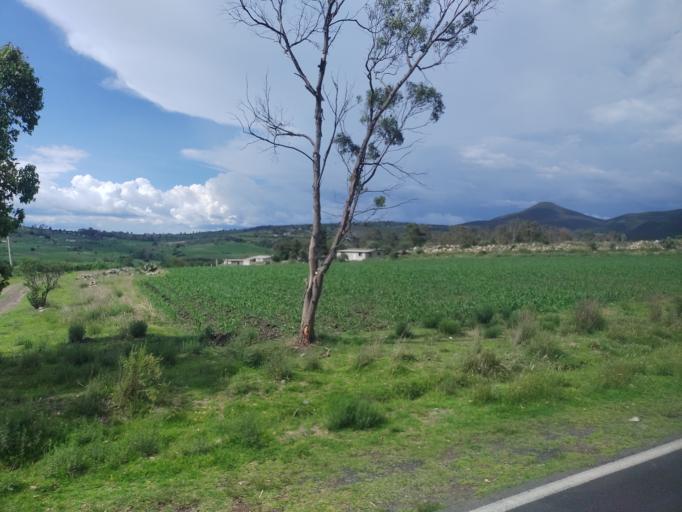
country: MX
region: Mexico
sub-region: Aculco
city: El Colorado
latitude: 20.1059
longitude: -99.7157
